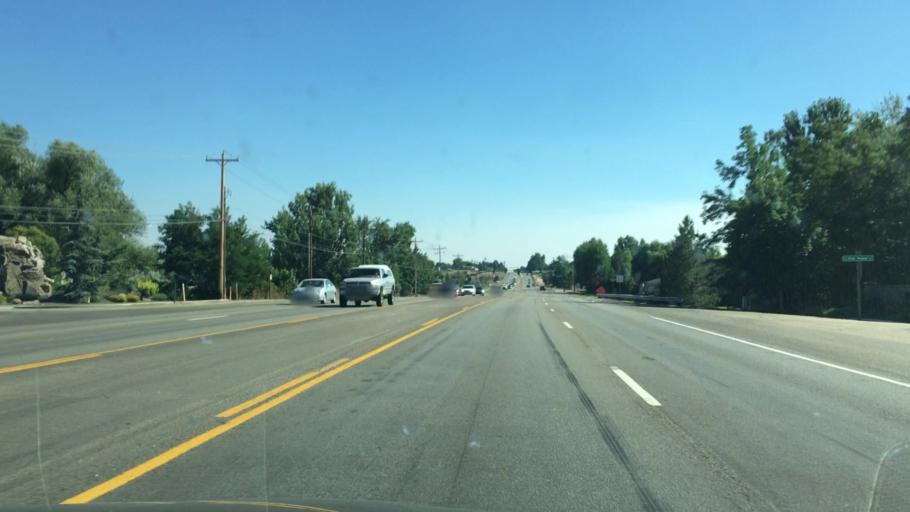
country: US
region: Idaho
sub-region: Ada County
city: Eagle
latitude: 43.6748
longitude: -116.3543
